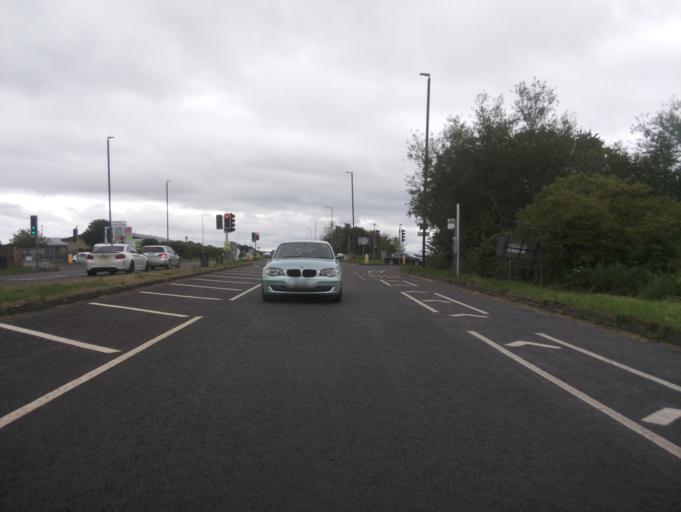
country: GB
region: England
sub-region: Gloucestershire
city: Tewkesbury
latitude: 51.9575
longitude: -2.1575
